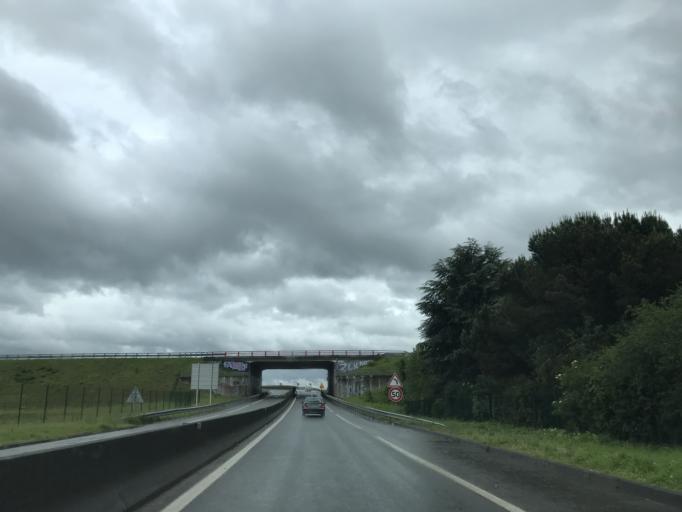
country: FR
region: Haute-Normandie
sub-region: Departement de l'Eure
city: Evreux
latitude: 49.0145
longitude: 1.1946
